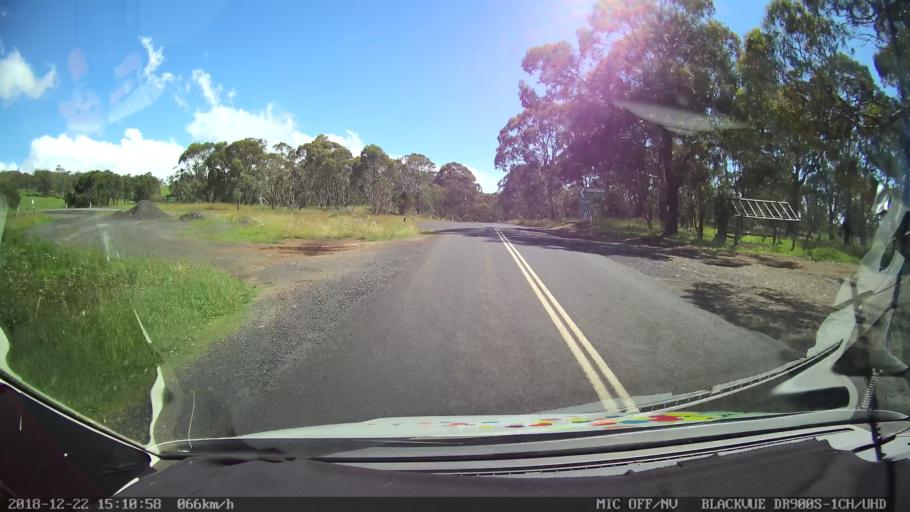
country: AU
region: New South Wales
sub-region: Bellingen
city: Dorrigo
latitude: -30.3405
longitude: 152.4061
